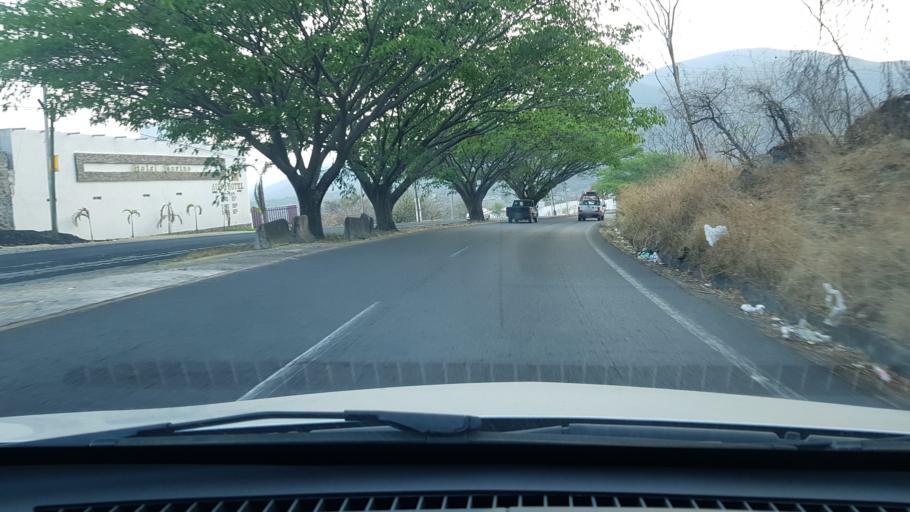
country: MX
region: Morelos
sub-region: Jiutepec
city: Independencia
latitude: 18.8605
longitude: -99.0975
